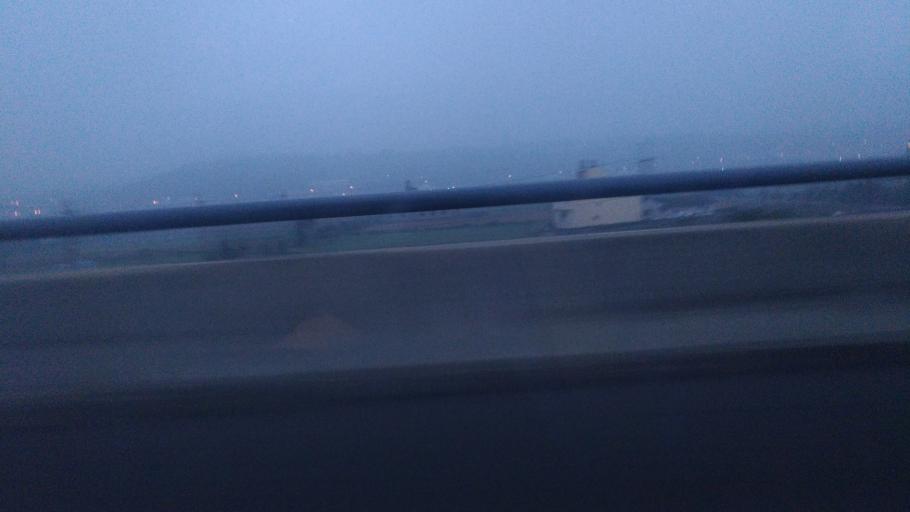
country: TW
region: Taiwan
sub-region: Miaoli
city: Miaoli
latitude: 24.4672
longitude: 120.6576
